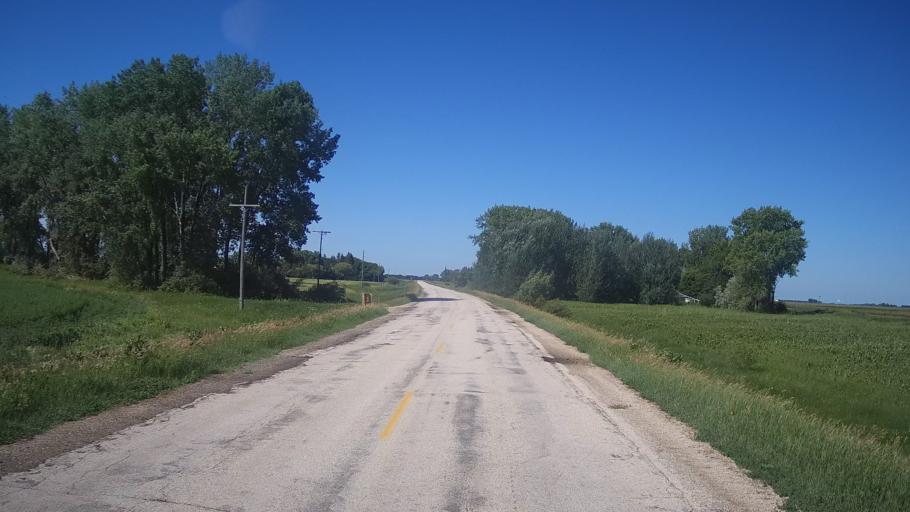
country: CA
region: Manitoba
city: Portage la Prairie
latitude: 50.0402
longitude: -98.0701
